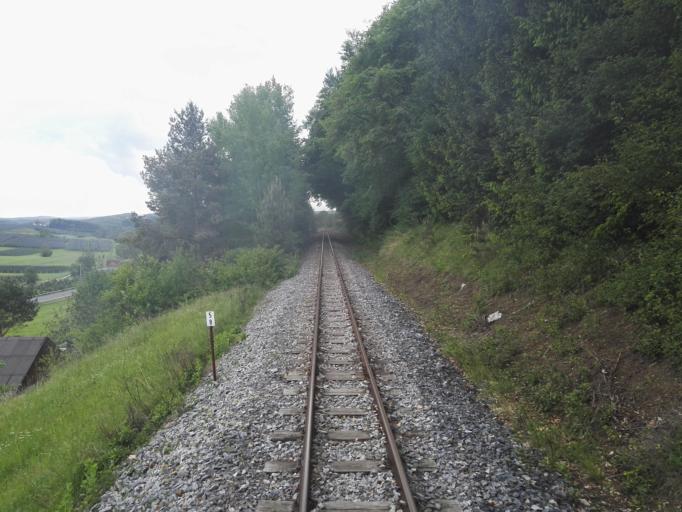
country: AT
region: Styria
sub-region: Politischer Bezirk Weiz
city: Puch bei Weiz
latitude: 47.2325
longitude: 15.6772
